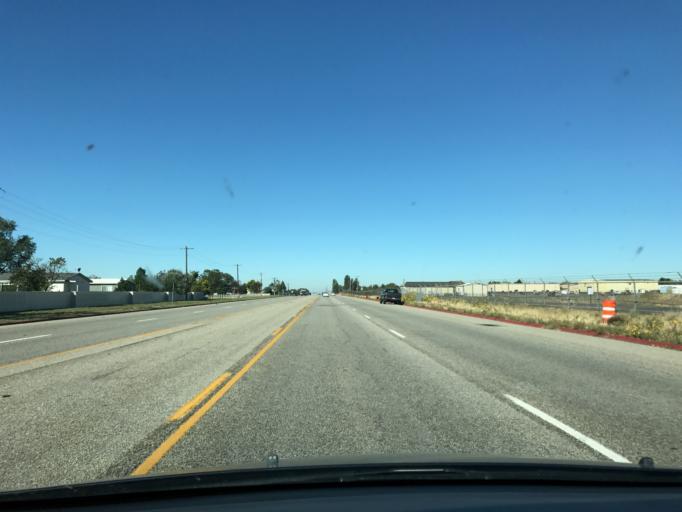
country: US
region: Utah
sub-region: Davis County
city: Hill Air Force Bace
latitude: 41.1036
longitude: -111.9653
